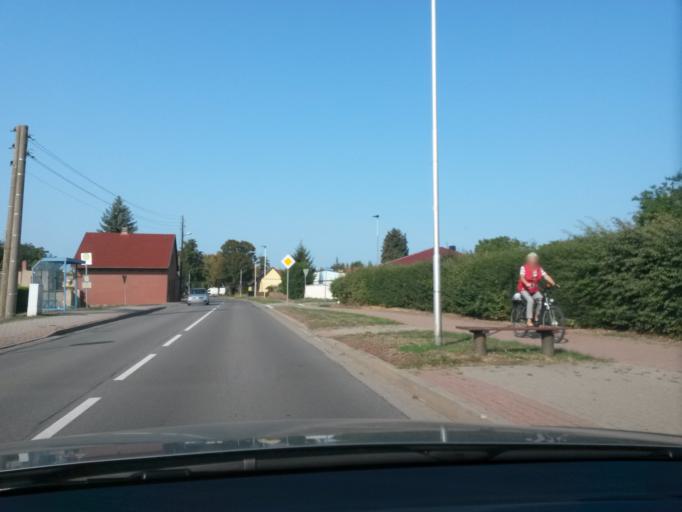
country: DE
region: Saxony-Anhalt
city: Tangermunde
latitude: 52.5350
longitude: 11.9498
